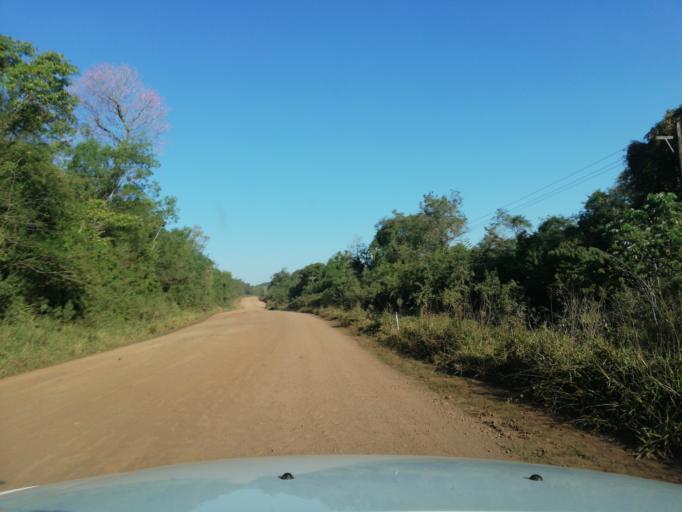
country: AR
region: Misiones
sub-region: Departamento de Candelaria
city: Candelaria
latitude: -27.5521
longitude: -55.7090
